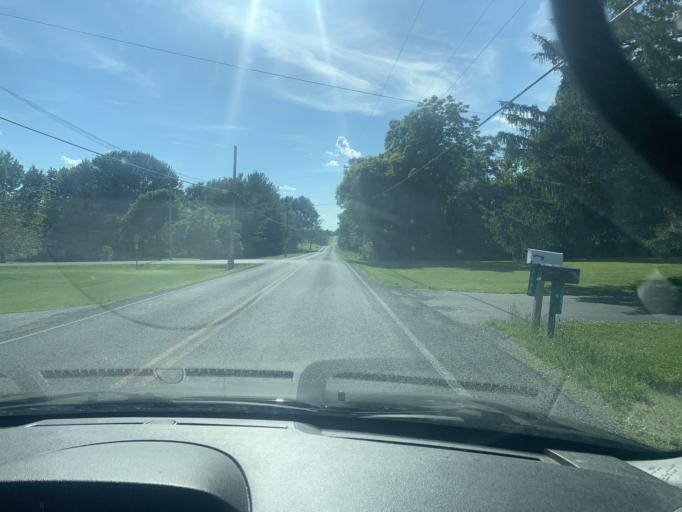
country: US
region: Ohio
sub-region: Logan County
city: Bellefontaine
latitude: 40.3493
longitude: -83.8028
